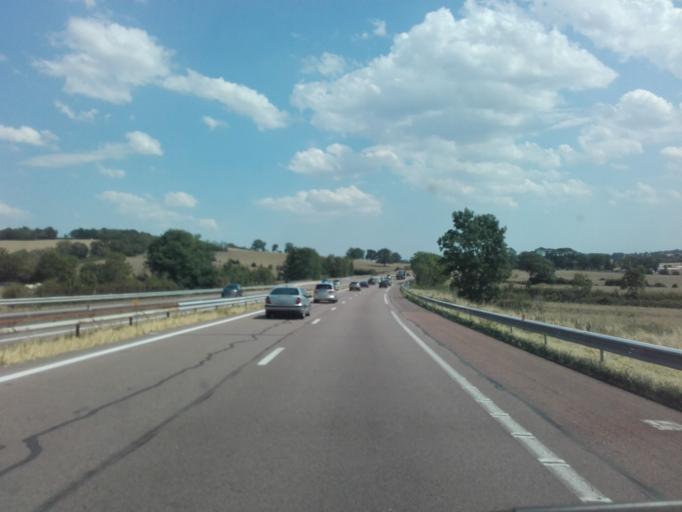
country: FR
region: Bourgogne
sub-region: Departement de l'Yonne
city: Avallon
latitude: 47.5501
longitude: 3.9624
